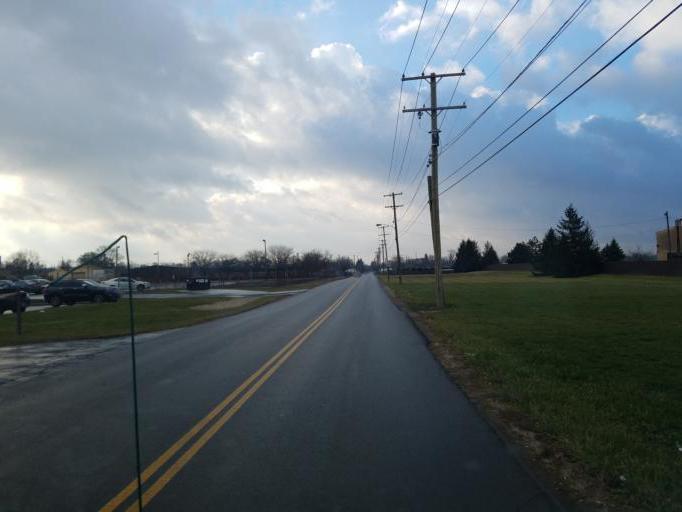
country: US
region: Ohio
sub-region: Marion County
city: Marion
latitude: 40.5987
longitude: -83.1376
